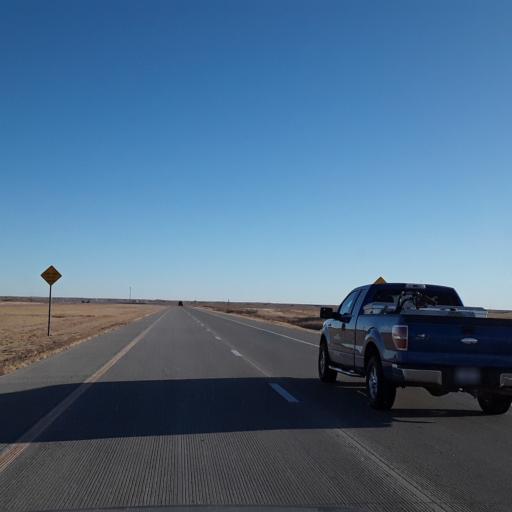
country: US
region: Kansas
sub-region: Seward County
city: Liberal
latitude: 37.1103
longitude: -100.7828
